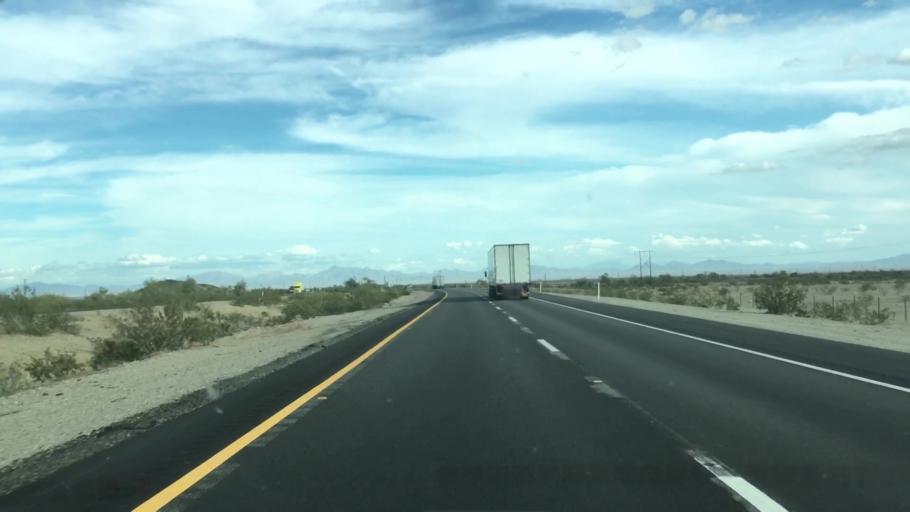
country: US
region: California
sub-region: Riverside County
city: Mesa Verde
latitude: 33.6092
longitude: -114.7747
